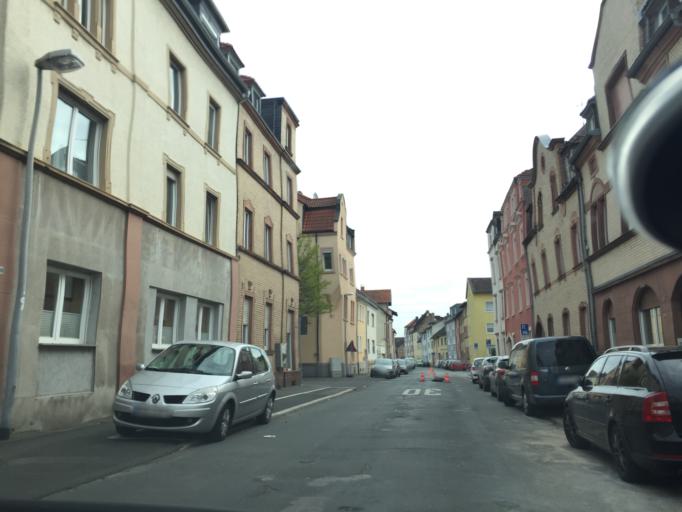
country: DE
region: Bavaria
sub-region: Regierungsbezirk Unterfranken
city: Aschaffenburg
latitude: 49.9834
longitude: 9.1318
